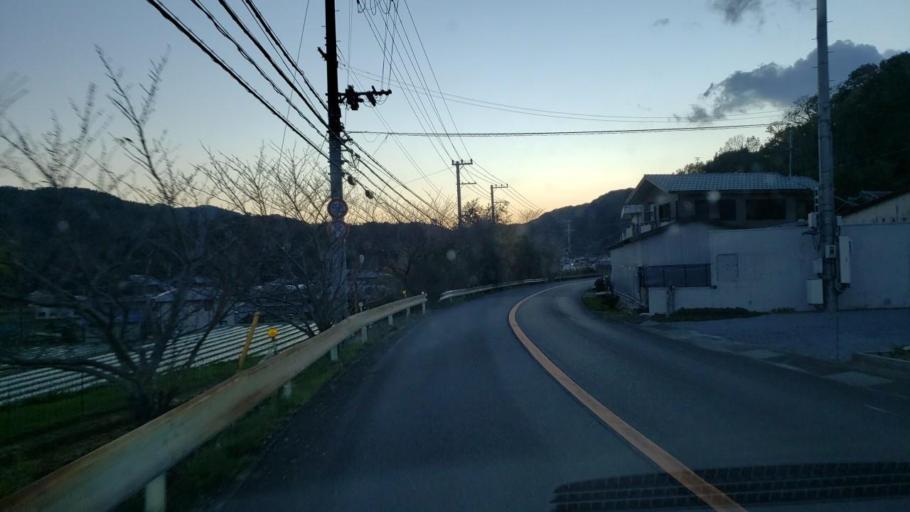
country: JP
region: Hyogo
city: Fukura
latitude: 34.2912
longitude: 134.7212
